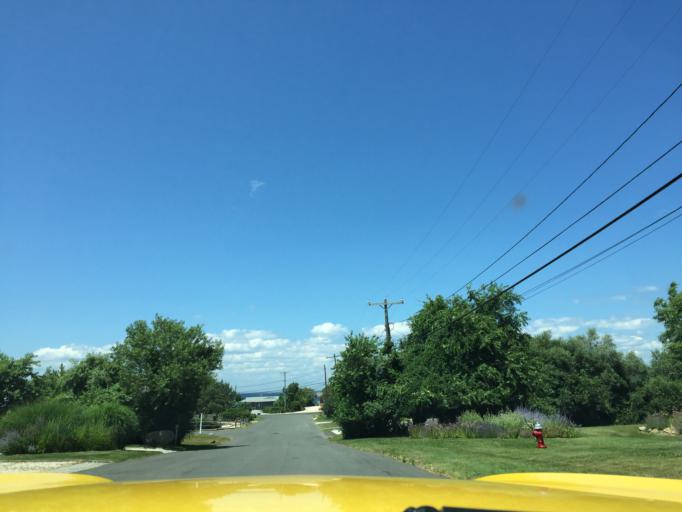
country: US
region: New York
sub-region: Suffolk County
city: Montauk
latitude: 41.0706
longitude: -71.9499
